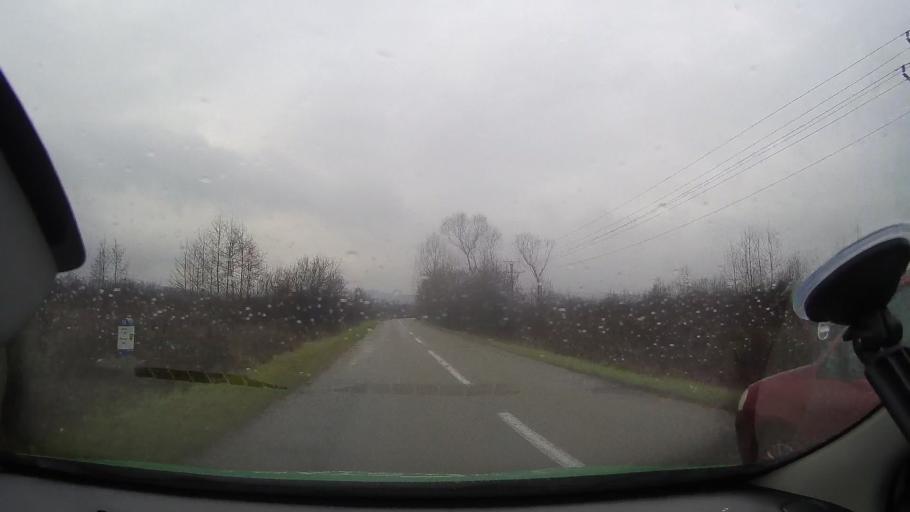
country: RO
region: Arad
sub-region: Comuna Ignesti
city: Ignesti
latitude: 46.3942
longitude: 22.1800
